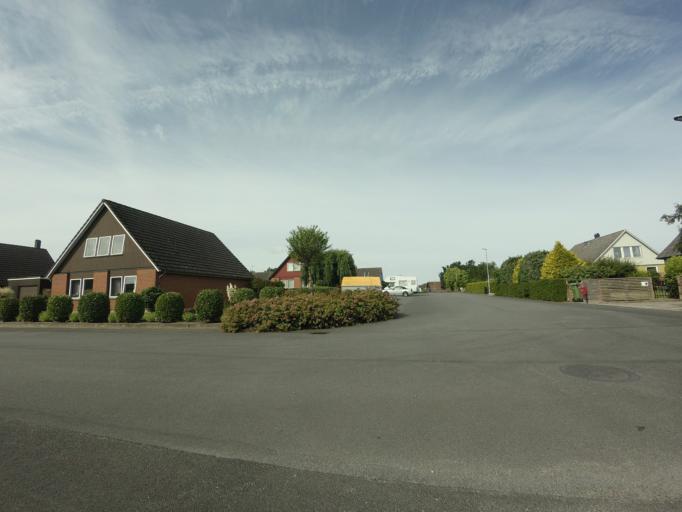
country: SE
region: Skane
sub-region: Simrishamns Kommun
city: Simrishamn
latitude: 55.5427
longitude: 14.3487
